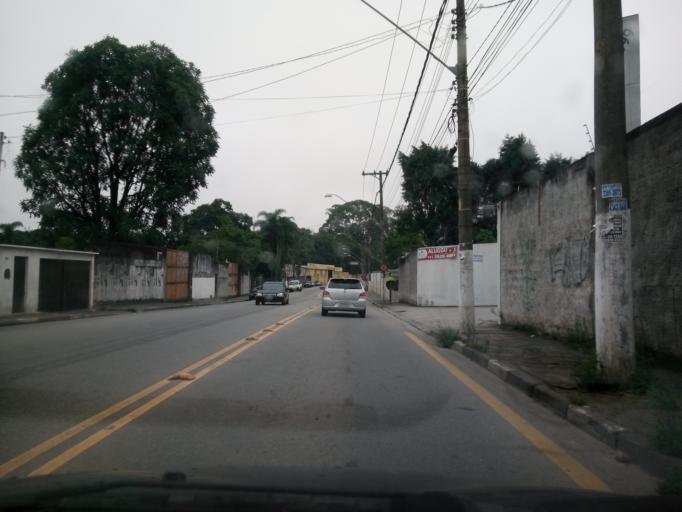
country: BR
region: Sao Paulo
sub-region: Sao Bernardo Do Campo
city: Sao Bernardo do Campo
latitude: -23.7367
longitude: -46.5676
